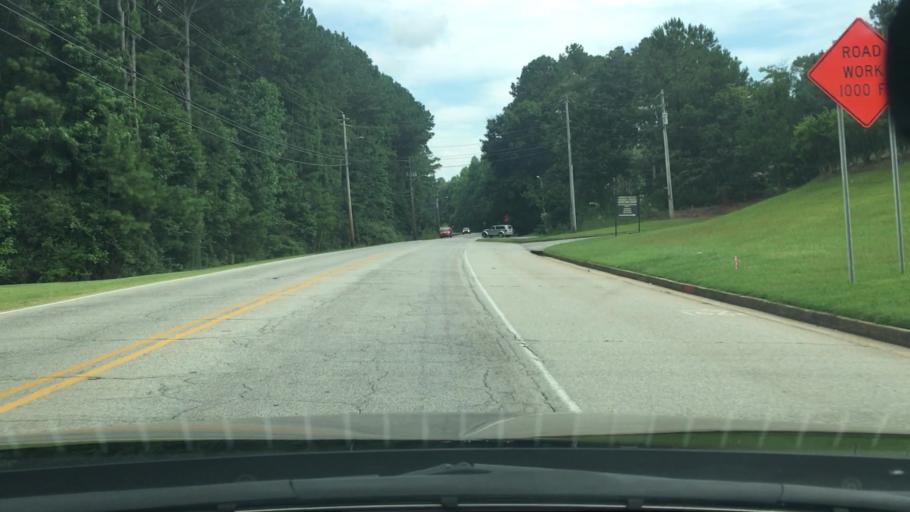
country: US
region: Georgia
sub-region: Coweta County
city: Newnan
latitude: 33.3816
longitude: -84.7821
